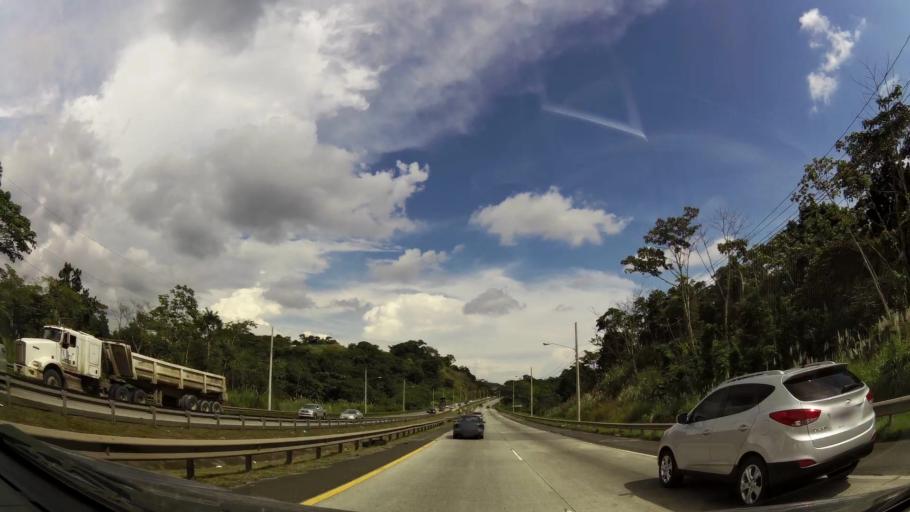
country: PA
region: Panama
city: Las Cumbres
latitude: 9.0409
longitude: -79.5606
